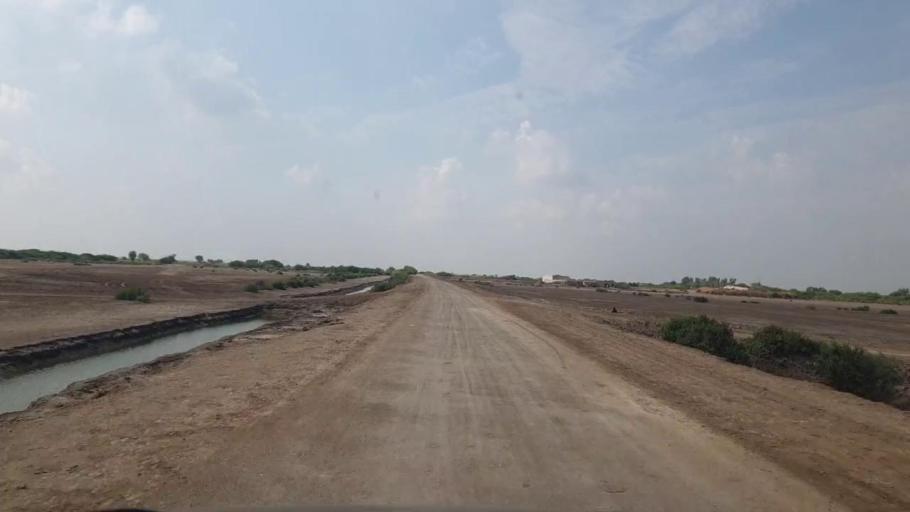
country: PK
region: Sindh
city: Badin
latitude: 24.5066
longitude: 68.6320
